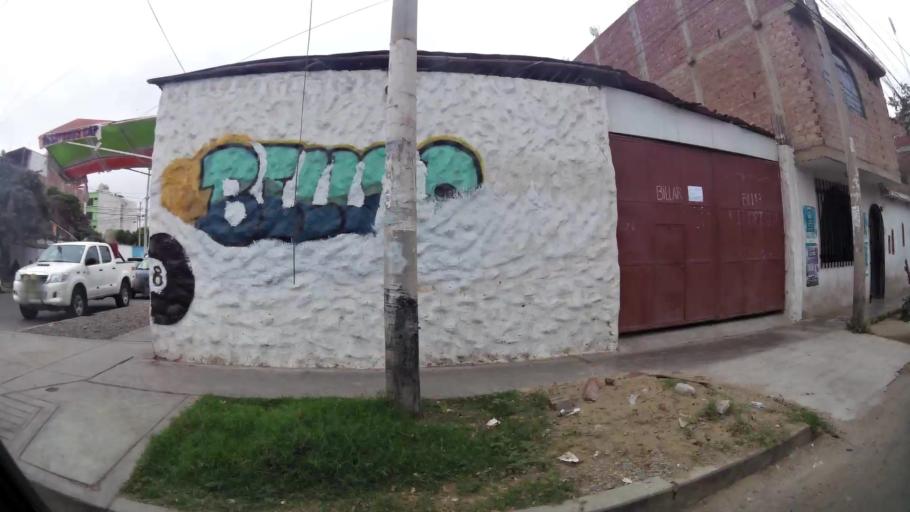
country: PE
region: La Libertad
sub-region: Provincia de Trujillo
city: Trujillo
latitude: -8.1084
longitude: -79.0439
